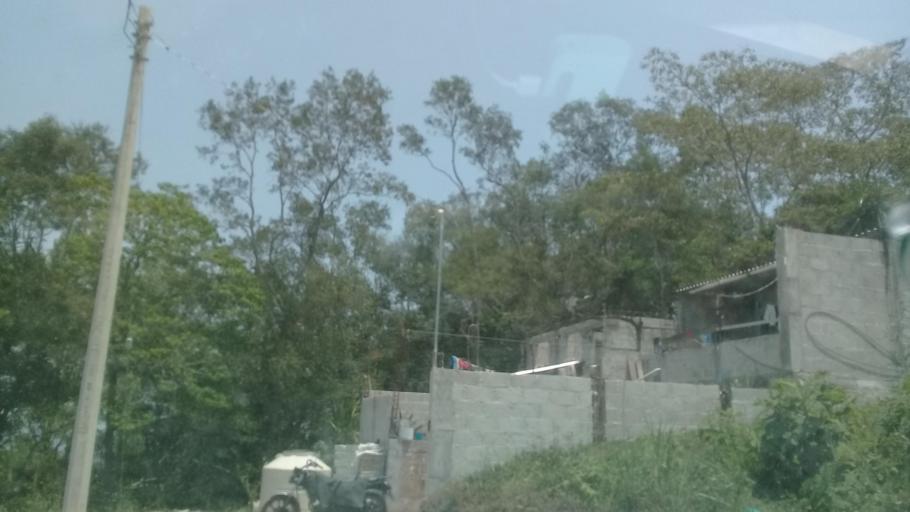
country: MX
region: Veracruz
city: El Castillo
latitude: 19.5619
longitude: -96.8558
